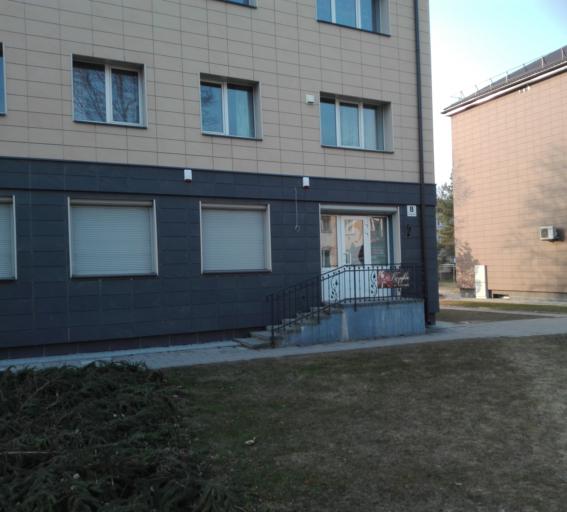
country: LT
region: Panevezys
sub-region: Birzai
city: Birzai
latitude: 56.2018
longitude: 24.7571
